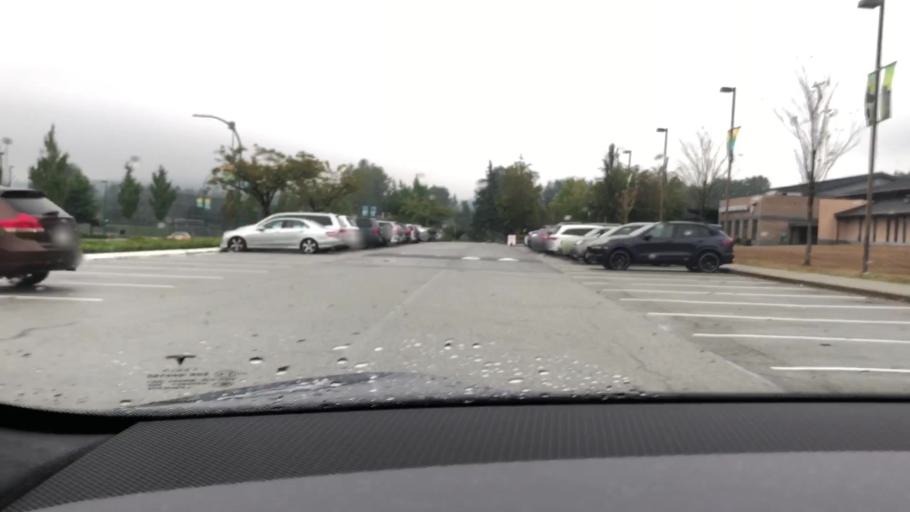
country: CA
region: British Columbia
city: Burnaby
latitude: 49.2510
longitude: -122.9662
